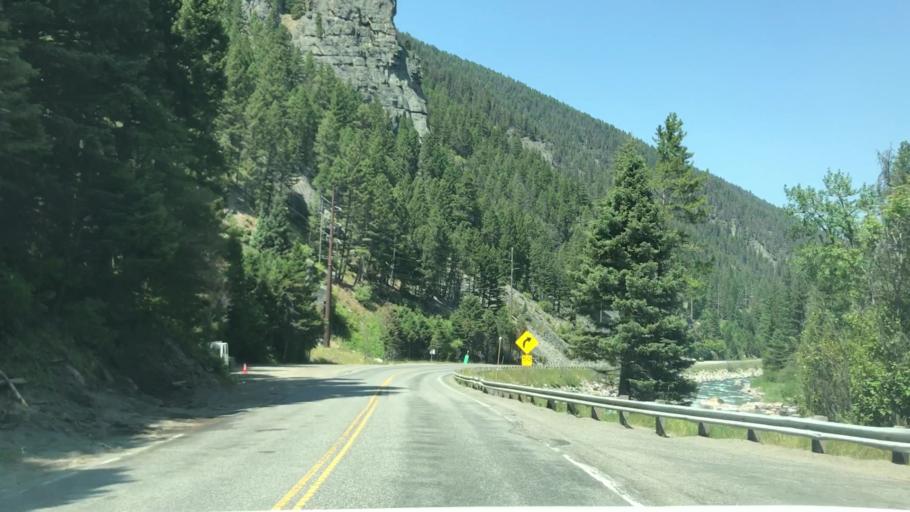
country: US
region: Montana
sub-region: Gallatin County
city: Big Sky
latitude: 45.4150
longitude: -111.2316
